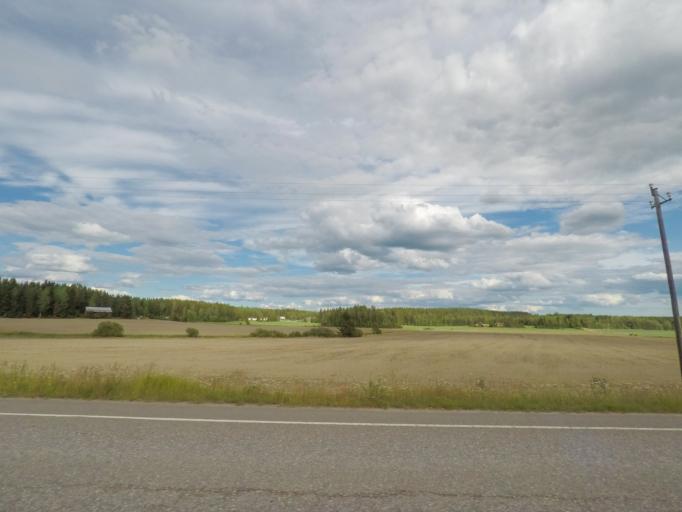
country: FI
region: Paijanne Tavastia
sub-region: Lahti
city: Hollola
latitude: 60.8589
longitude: 25.5001
